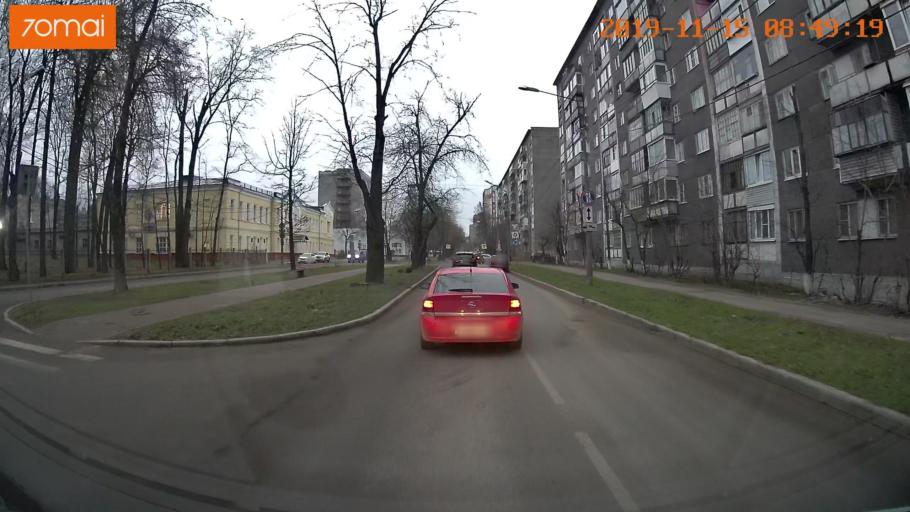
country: RU
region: Vologda
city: Cherepovets
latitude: 59.1230
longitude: 37.9217
